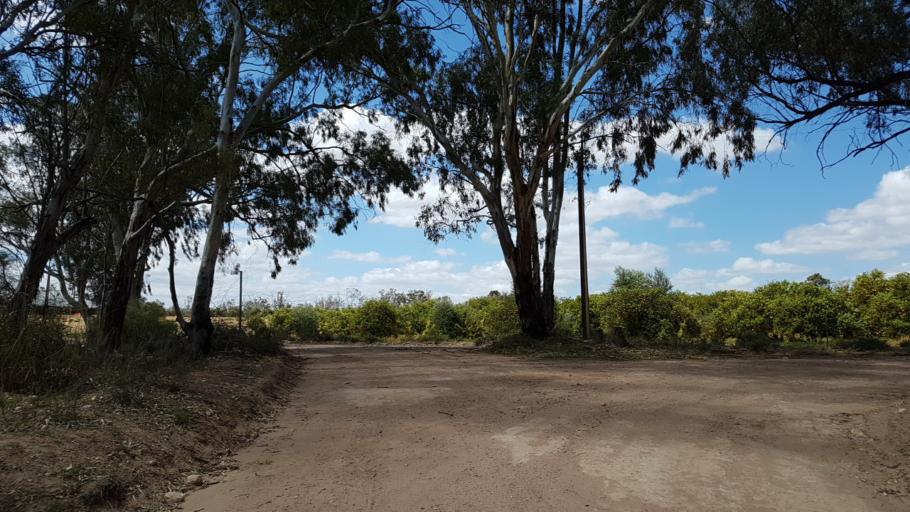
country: AU
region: South Australia
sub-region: Loxton Waikerie
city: Waikerie
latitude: -34.1672
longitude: 140.0251
